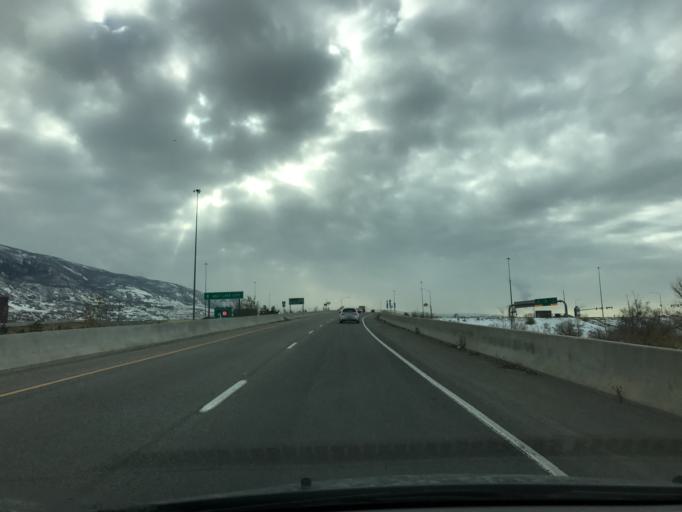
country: US
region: Utah
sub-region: Davis County
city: Farmington
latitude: 40.9932
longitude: -111.9043
